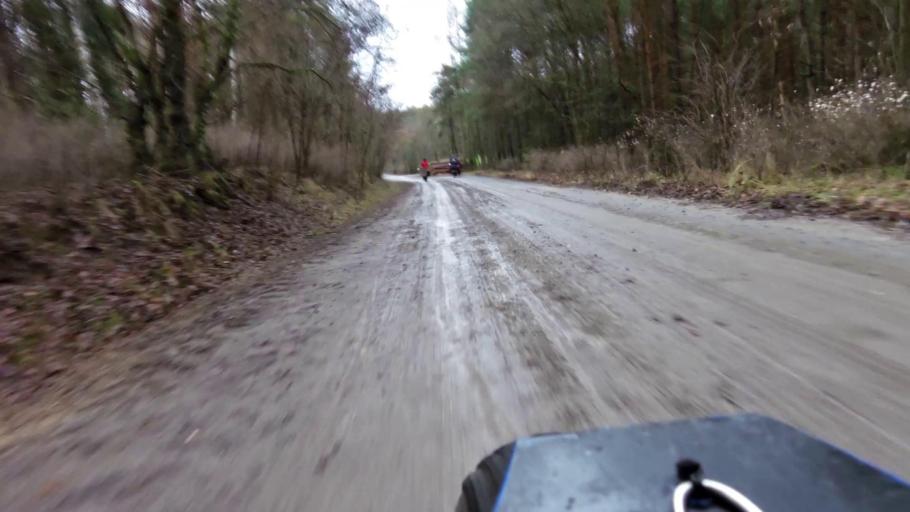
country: PL
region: Lubusz
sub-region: Powiat gorzowski
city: Witnica
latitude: 52.6931
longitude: 14.8511
